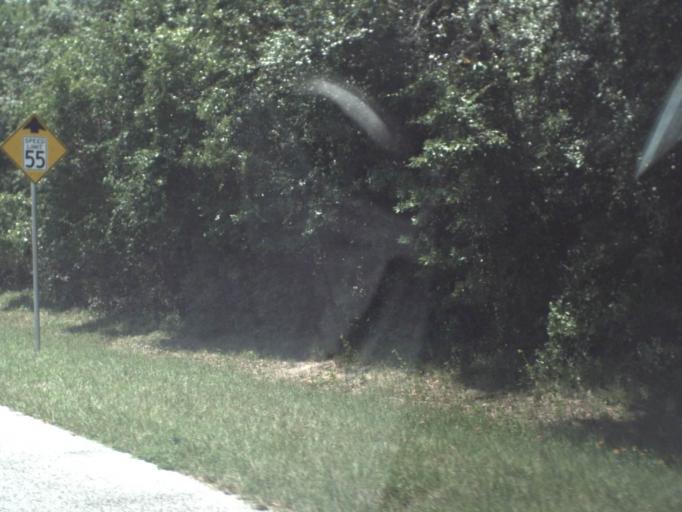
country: US
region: Florida
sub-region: Flagler County
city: Palm Coast
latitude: 29.6702
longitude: -81.2899
